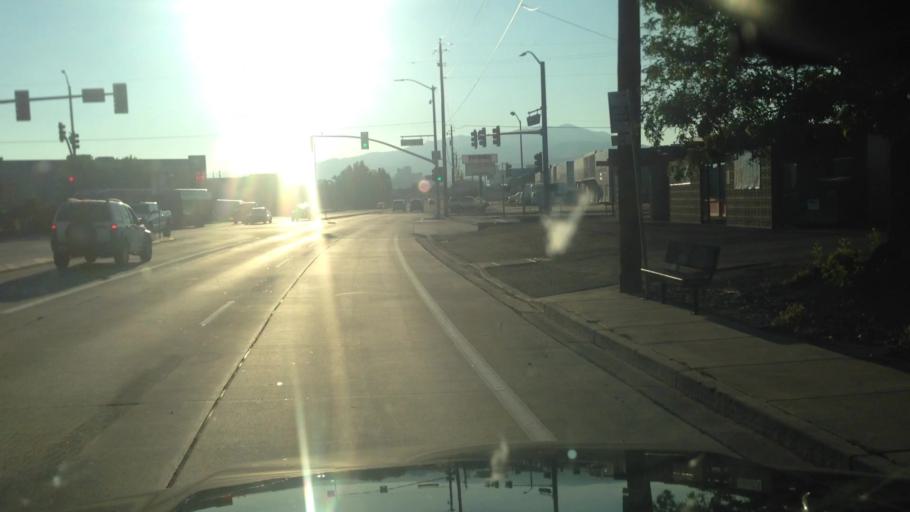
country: US
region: Nevada
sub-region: Washoe County
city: Sparks
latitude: 39.5174
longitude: -119.7767
